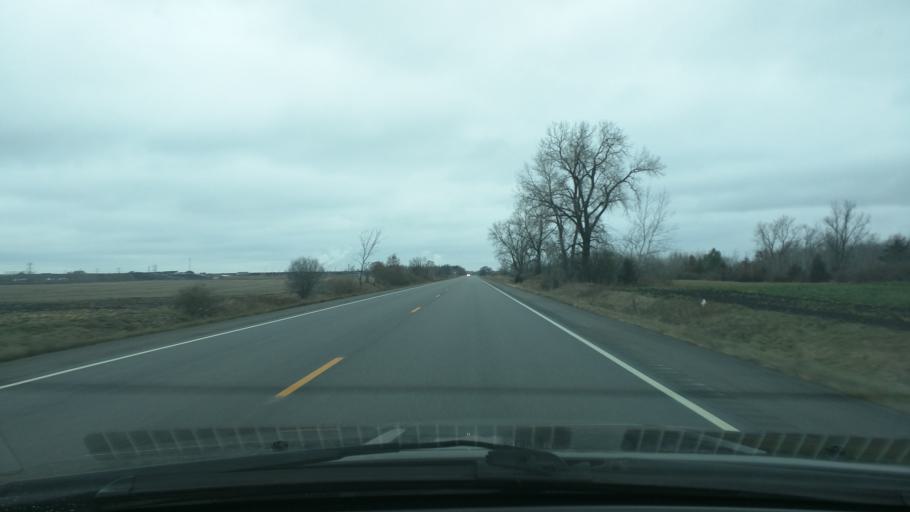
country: US
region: Minnesota
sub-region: Washington County
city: Cottage Grove
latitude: 44.7459
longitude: -92.9925
